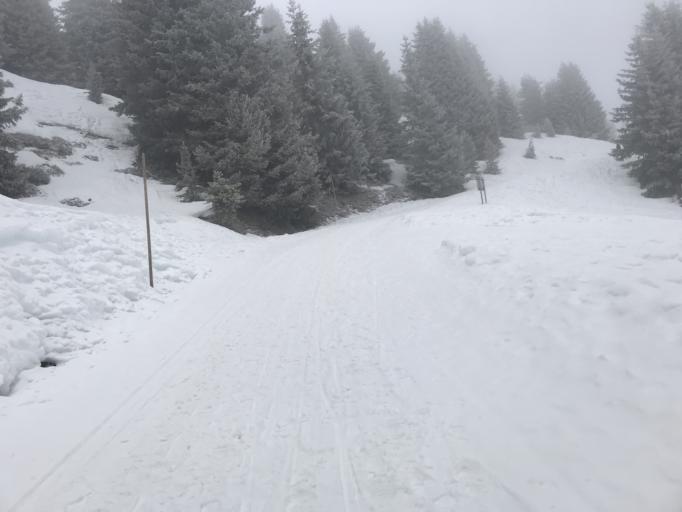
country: IT
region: Trentino-Alto Adige
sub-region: Bolzano
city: San Pietro
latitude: 46.6849
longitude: 11.7134
